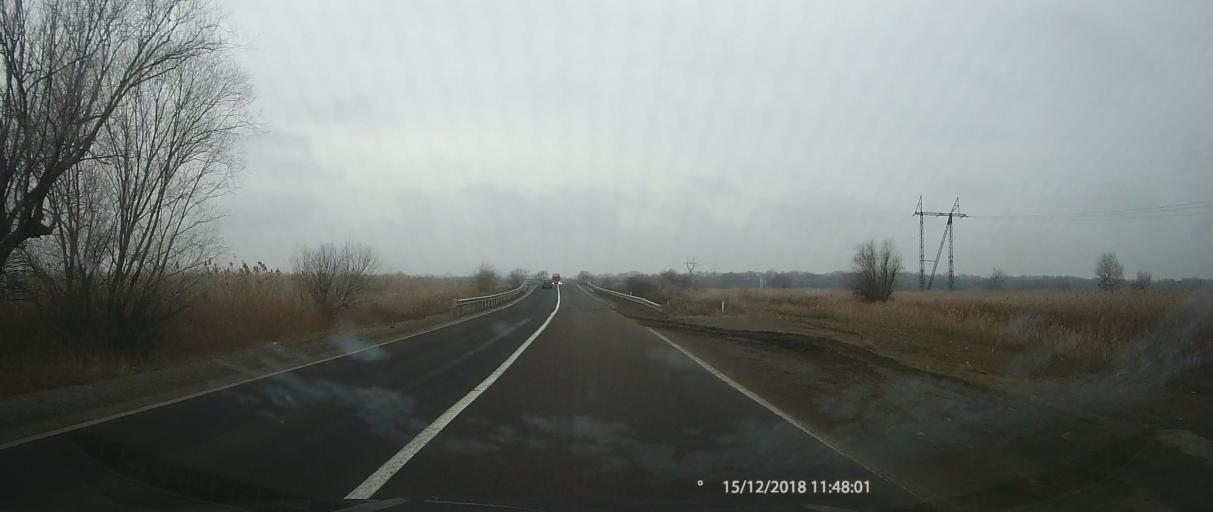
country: UA
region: Odessa
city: Bilyayivka
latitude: 46.4140
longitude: 30.1579
